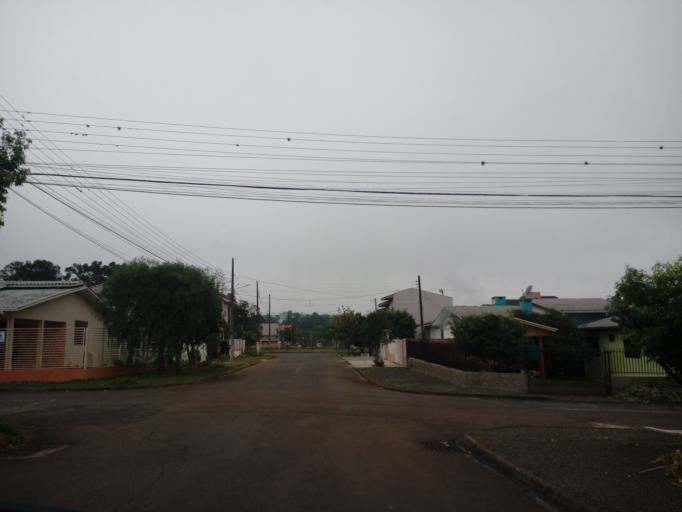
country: BR
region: Santa Catarina
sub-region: Chapeco
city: Chapeco
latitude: -27.1005
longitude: -52.6673
